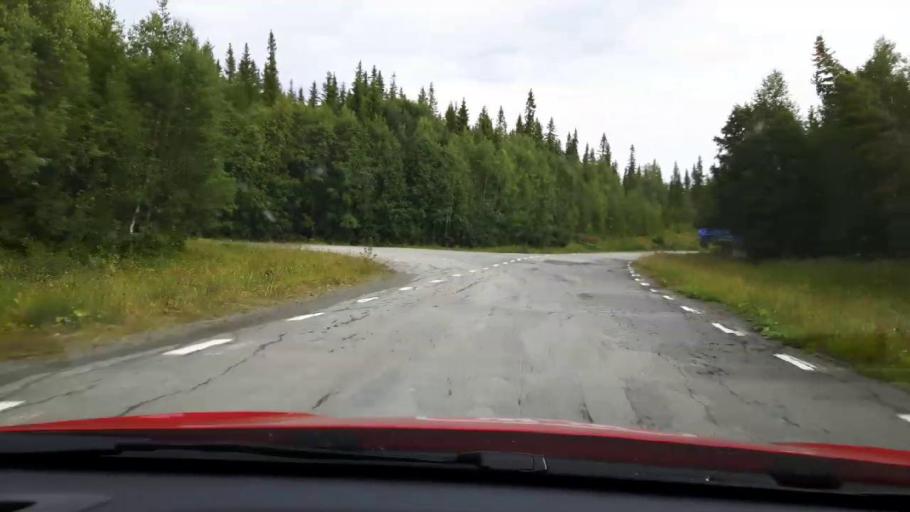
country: SE
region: Jaemtland
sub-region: Are Kommun
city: Are
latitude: 63.7371
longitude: 13.0188
